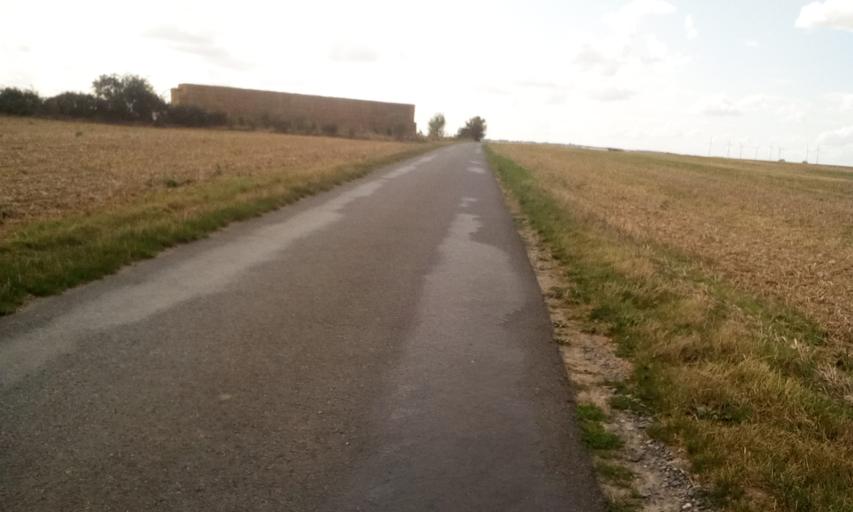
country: FR
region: Lower Normandy
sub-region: Departement du Calvados
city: Saint-Sylvain
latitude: 49.0745
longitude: -0.2015
